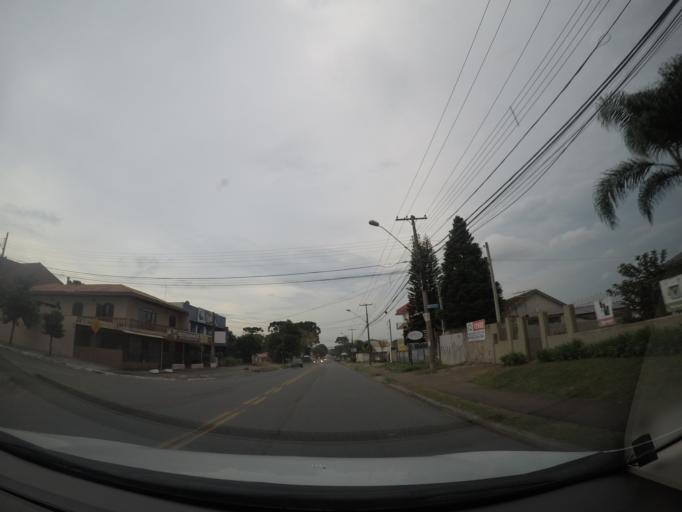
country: BR
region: Parana
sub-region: Sao Jose Dos Pinhais
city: Sao Jose dos Pinhais
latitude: -25.5249
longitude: -49.2365
